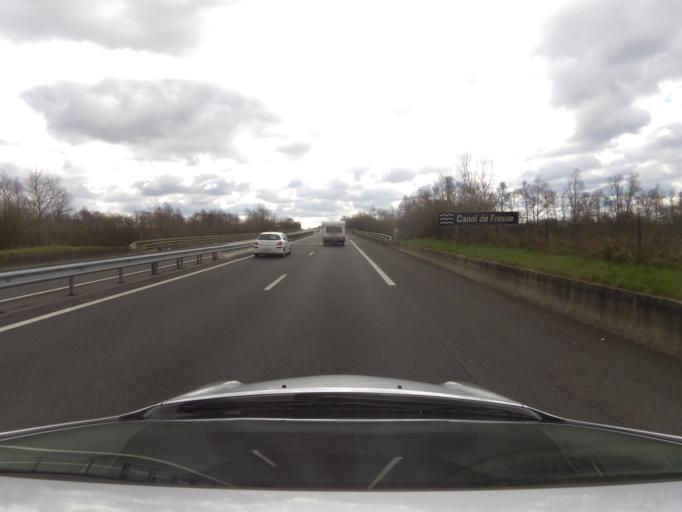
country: FR
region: Picardie
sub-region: Departement de la Somme
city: Quend
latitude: 50.3337
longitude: 1.7017
